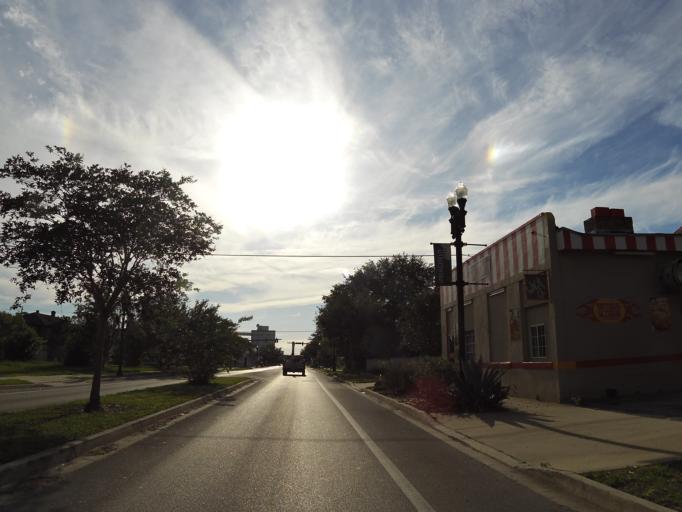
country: US
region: Florida
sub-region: Duval County
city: Jacksonville
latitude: 30.3461
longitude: -81.6573
